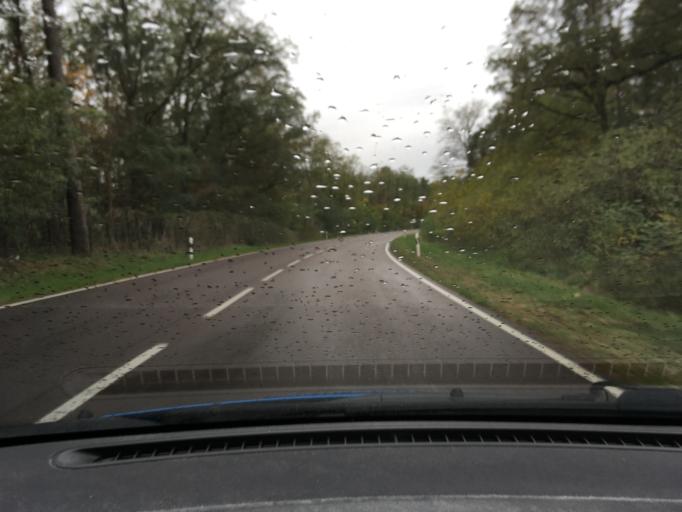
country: DE
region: Saxony-Anhalt
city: Rosslau
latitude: 51.8838
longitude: 12.2945
